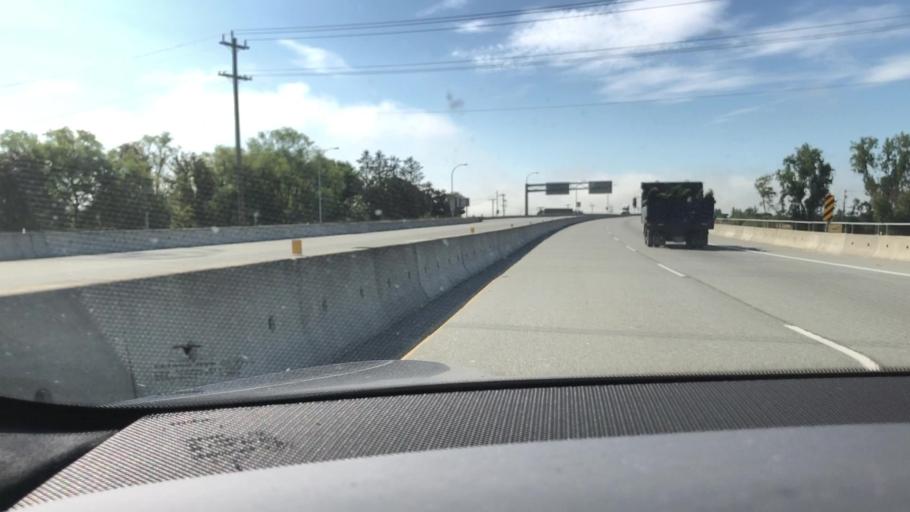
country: CA
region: British Columbia
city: Ladner
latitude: 49.0923
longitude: -123.0253
